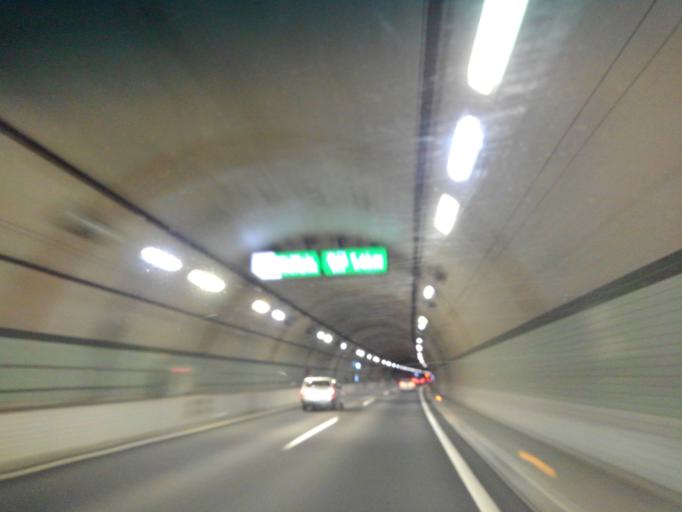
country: JP
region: Tokyo
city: Hachioji
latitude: 35.6366
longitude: 139.2573
